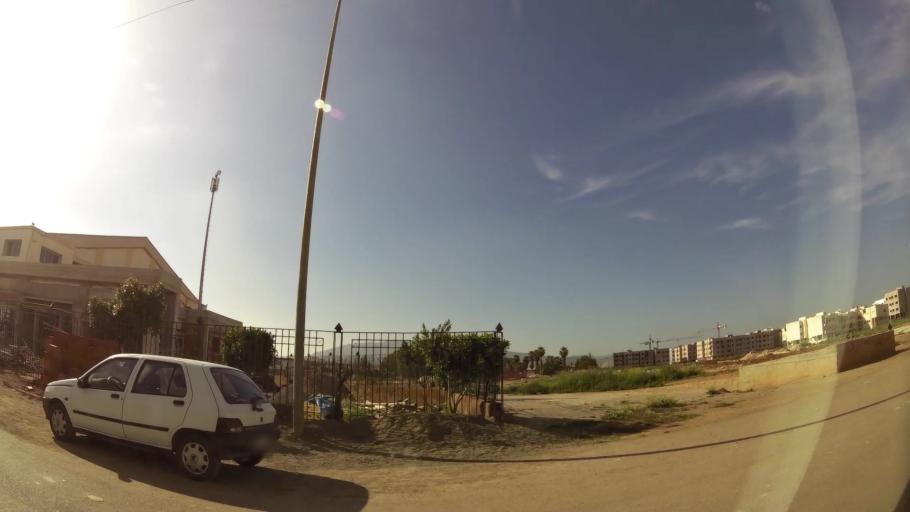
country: MA
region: Fes-Boulemane
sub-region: Fes
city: Fes
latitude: 34.0228
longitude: -5.0300
